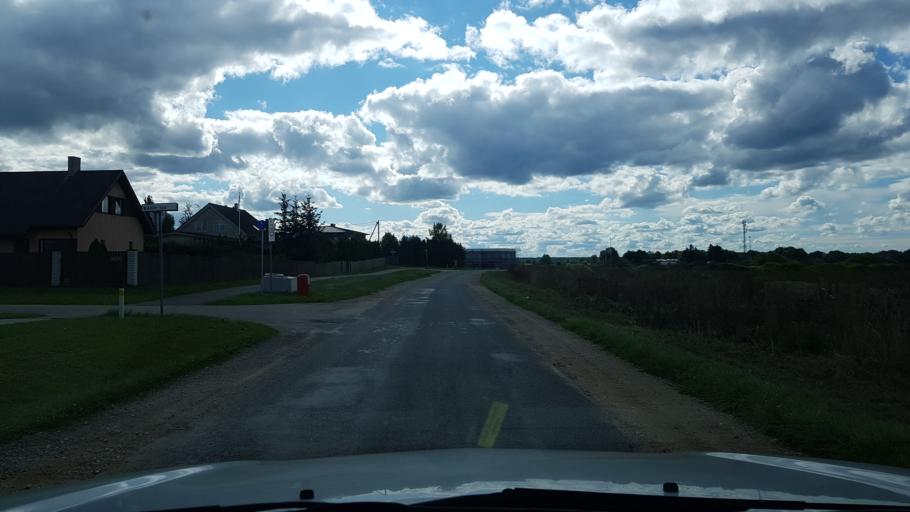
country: EE
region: Harju
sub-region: Tallinna linn
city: Tallinn
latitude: 59.3844
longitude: 24.8122
